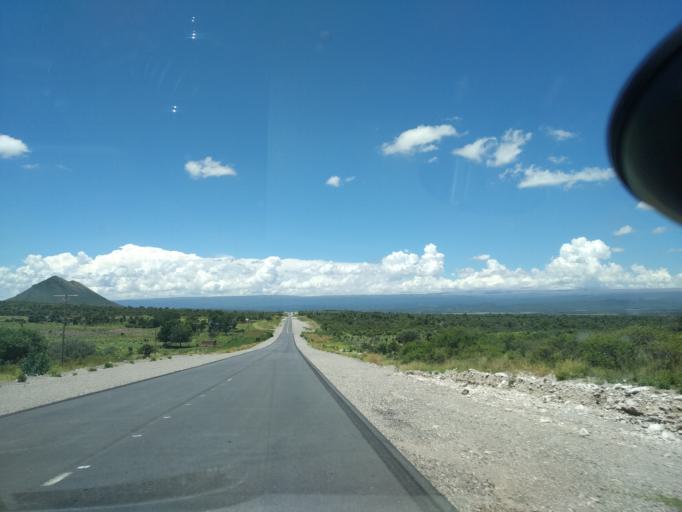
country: AR
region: Cordoba
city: Salsacate
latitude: -31.3619
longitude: -65.1922
